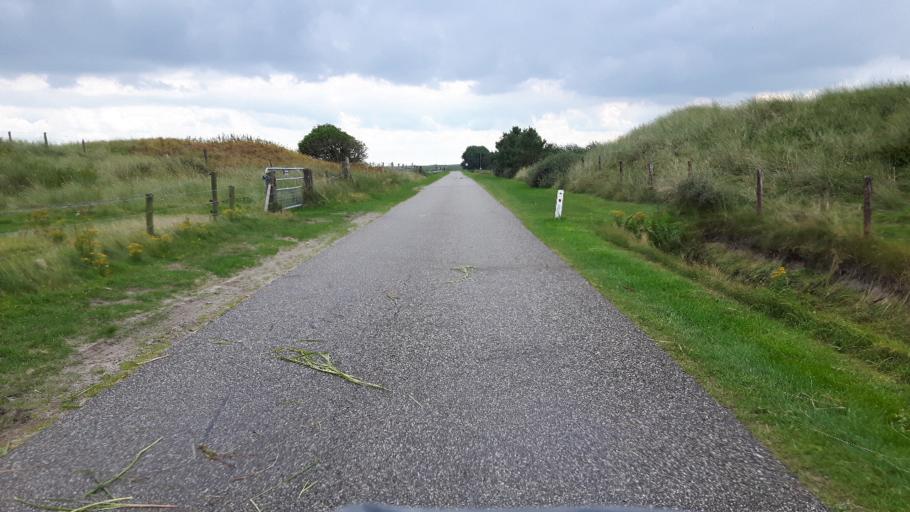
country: NL
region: Friesland
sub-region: Gemeente Ameland
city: Nes
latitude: 53.4519
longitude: 5.8176
